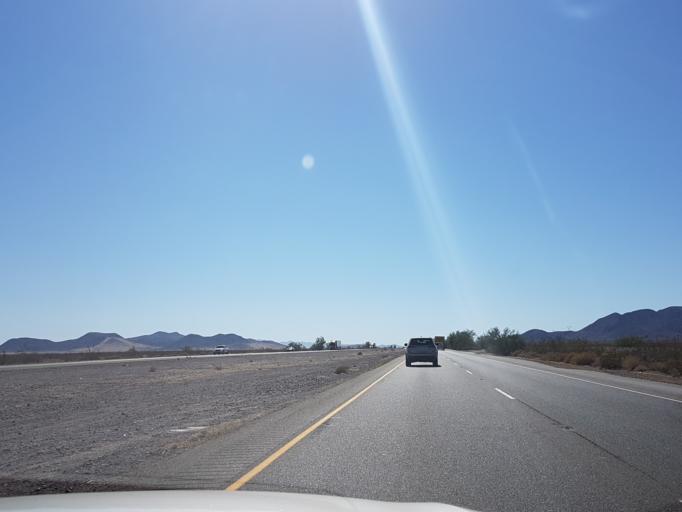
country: US
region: California
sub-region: San Bernardino County
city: Fort Irwin
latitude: 35.1769
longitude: -116.1720
